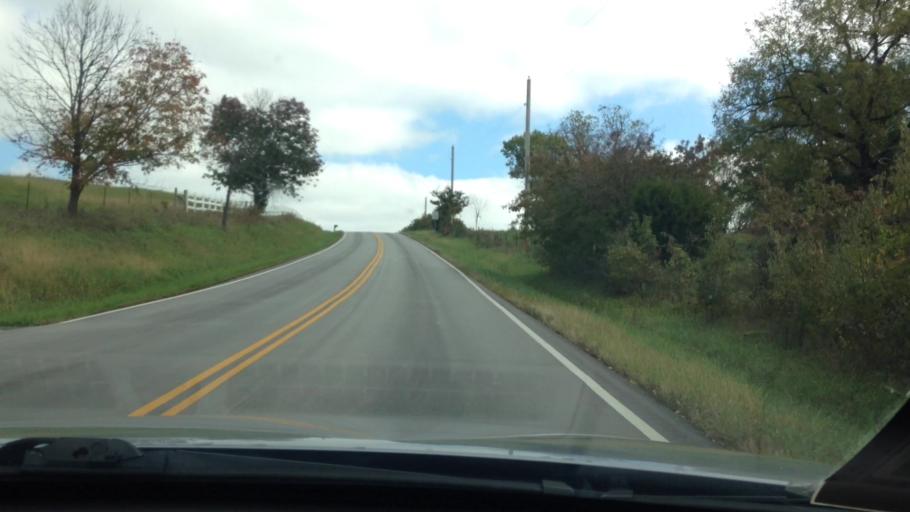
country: US
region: Missouri
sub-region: Platte County
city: Weatherby Lake
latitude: 39.2488
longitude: -94.7843
